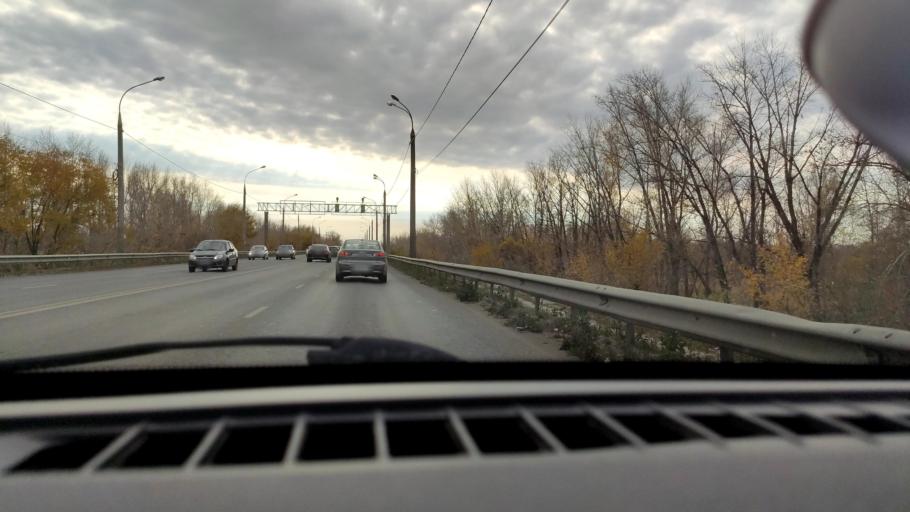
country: RU
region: Samara
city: Samara
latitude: 53.1504
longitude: 50.1861
